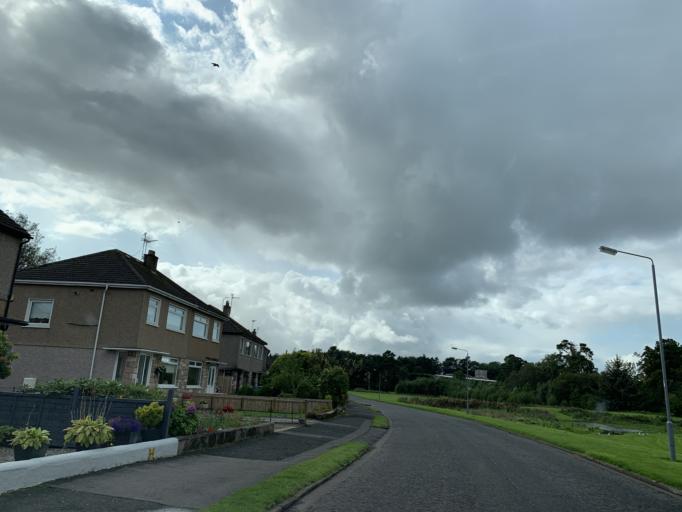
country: GB
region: Scotland
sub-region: East Renfrewshire
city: Newton Mearns
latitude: 55.7847
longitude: -4.3242
